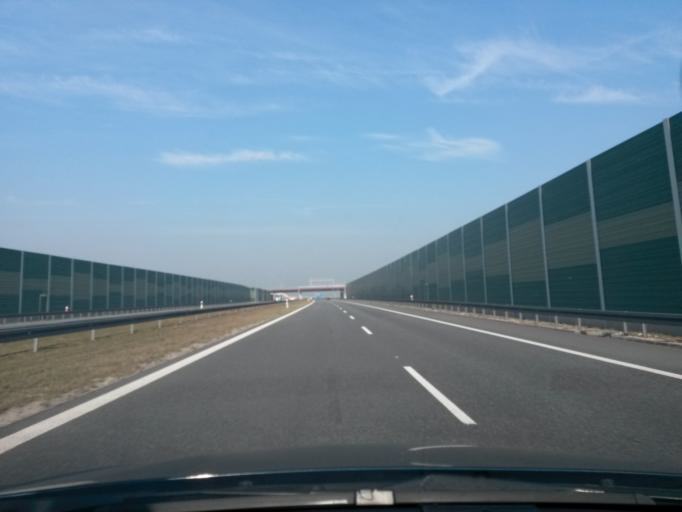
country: PL
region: Lodz Voivodeship
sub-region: Powiat kutnowski
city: Krzyzanow
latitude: 52.2162
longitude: 19.4757
